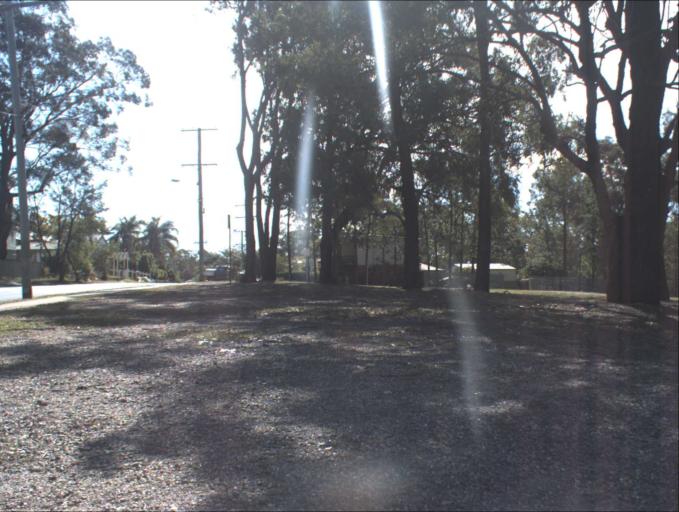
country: AU
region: Queensland
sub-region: Logan
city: Slacks Creek
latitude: -27.6427
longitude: 153.1325
